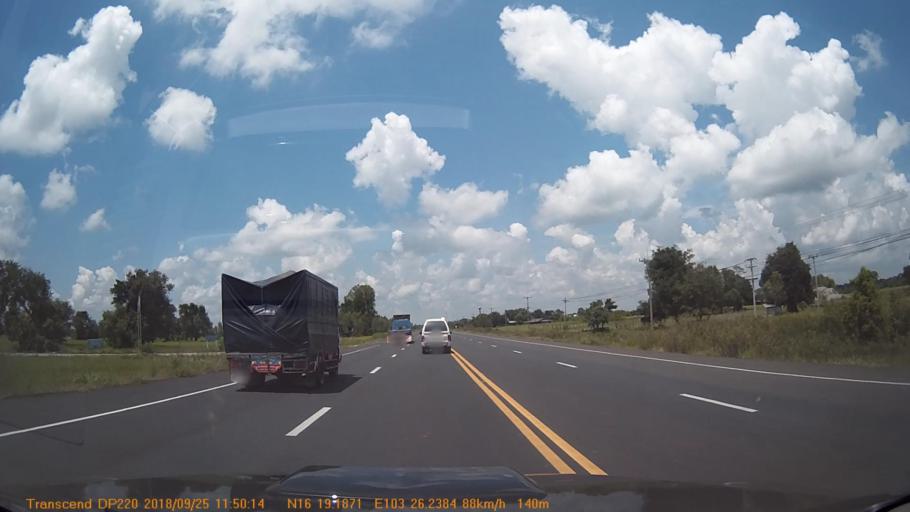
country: TH
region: Kalasin
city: Khong Chai
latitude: 16.3197
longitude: 103.4374
